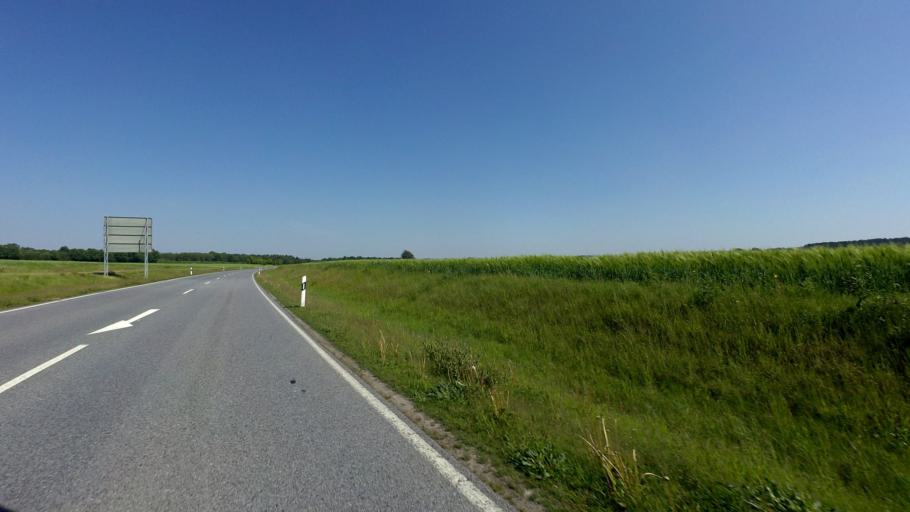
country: DE
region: Saxony
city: Nebelschutz
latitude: 51.2667
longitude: 14.1440
